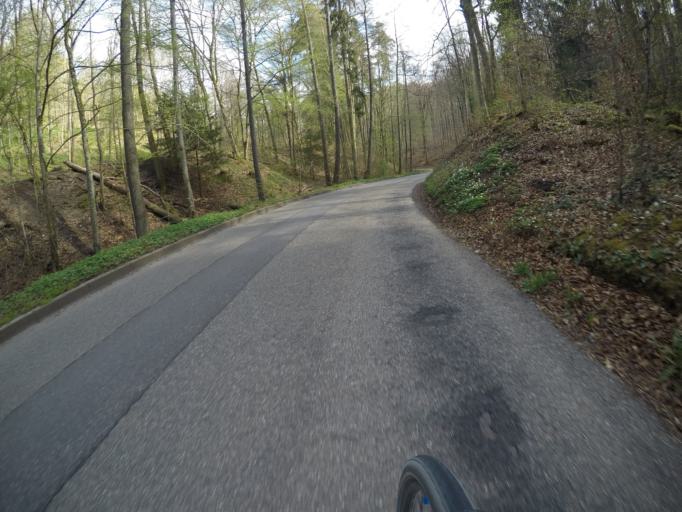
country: DE
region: Baden-Wuerttemberg
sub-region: Regierungsbezirk Stuttgart
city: Gerlingen
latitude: 48.7702
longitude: 9.0547
